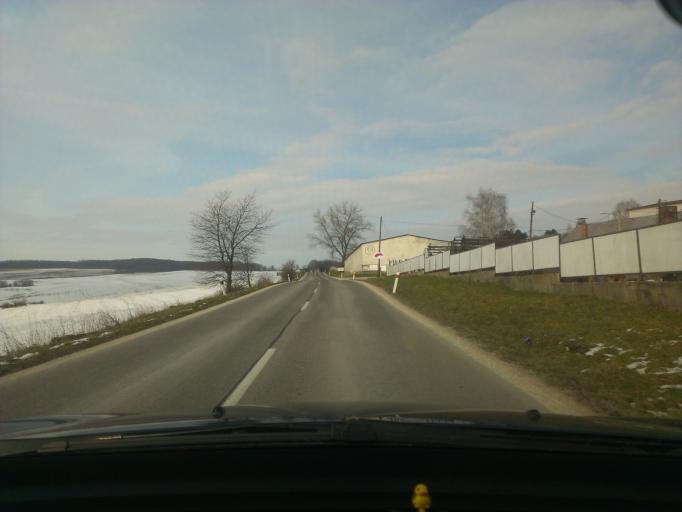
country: SK
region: Nitriansky
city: Stara Tura
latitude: 48.7102
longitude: 17.6849
